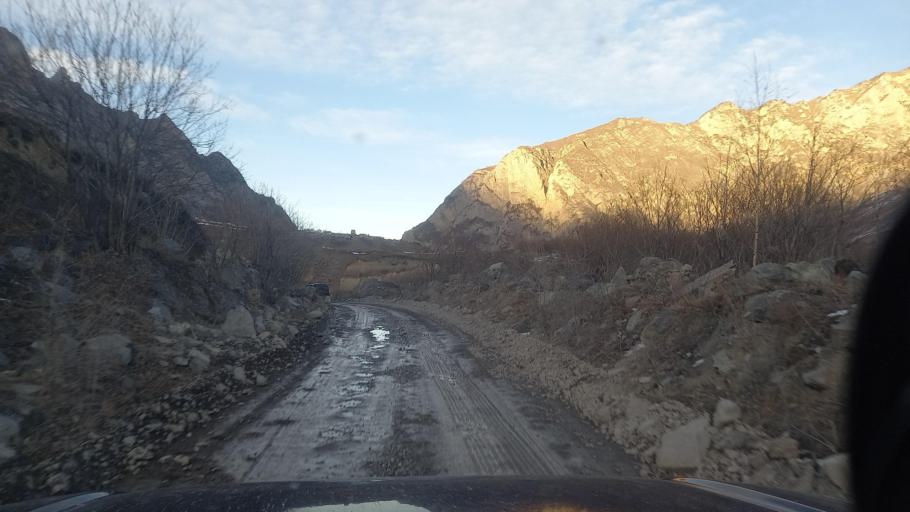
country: RU
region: Ingushetiya
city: Dzhayrakh
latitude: 42.8444
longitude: 44.5154
